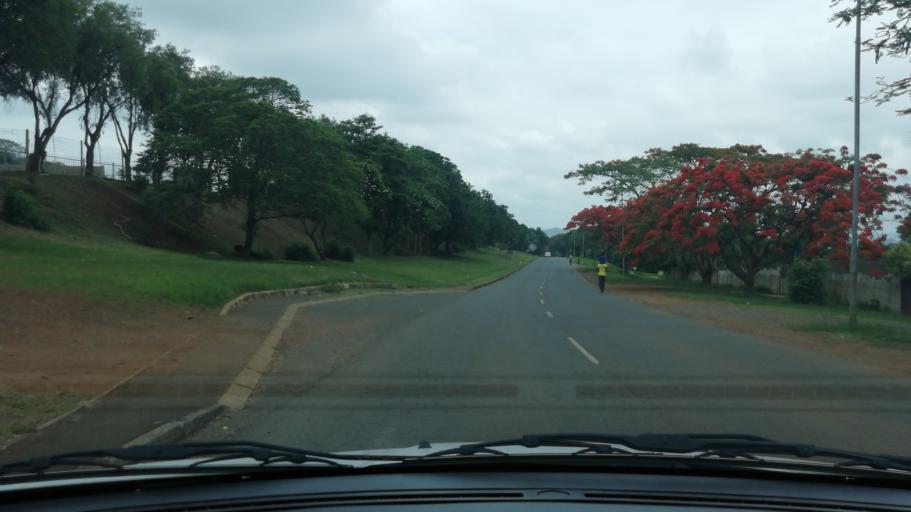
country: ZA
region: KwaZulu-Natal
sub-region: uThungulu District Municipality
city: Empangeni
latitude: -28.7531
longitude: 31.8849
